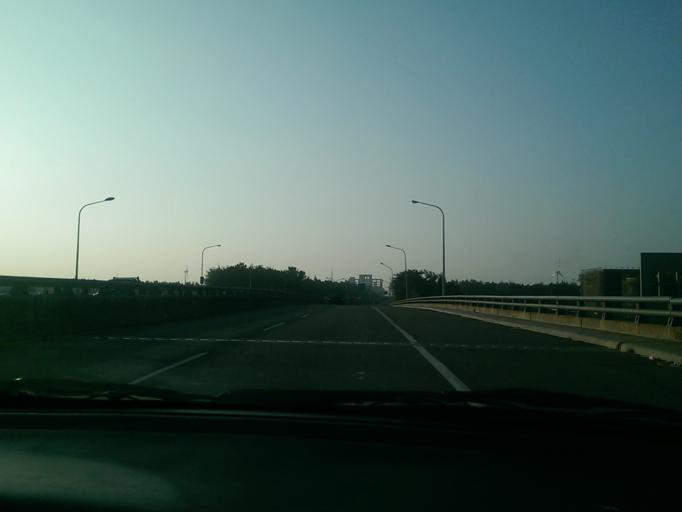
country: TW
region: Taiwan
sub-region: Changhua
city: Chang-hua
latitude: 24.1415
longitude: 120.4449
